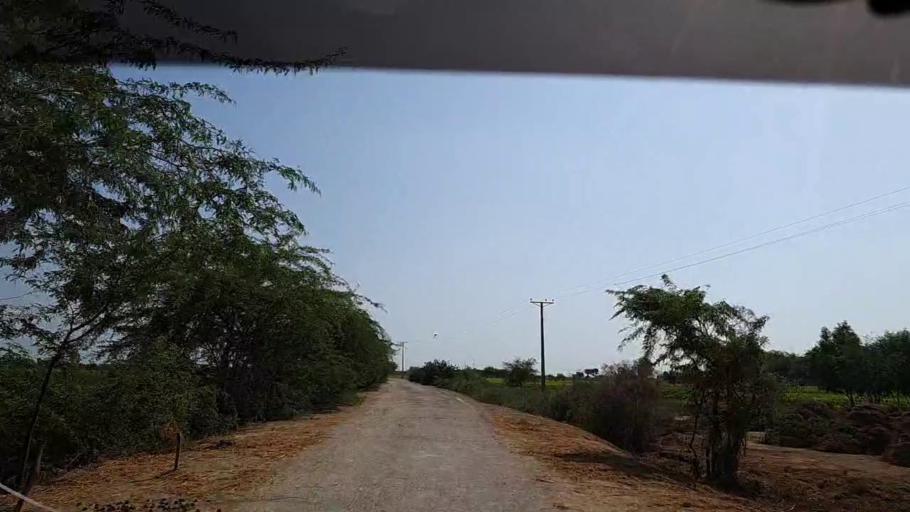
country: PK
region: Sindh
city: Badin
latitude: 24.6427
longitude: 68.7879
